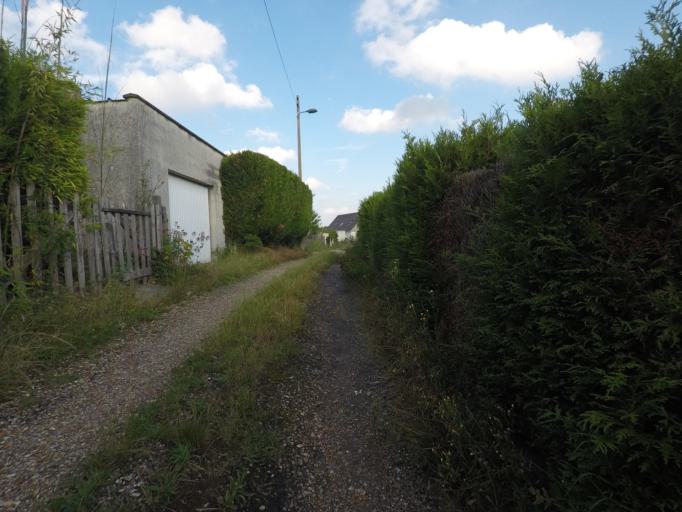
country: FR
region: Haute-Normandie
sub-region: Departement de la Seine-Maritime
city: Bihorel
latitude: 49.4444
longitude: 1.1198
